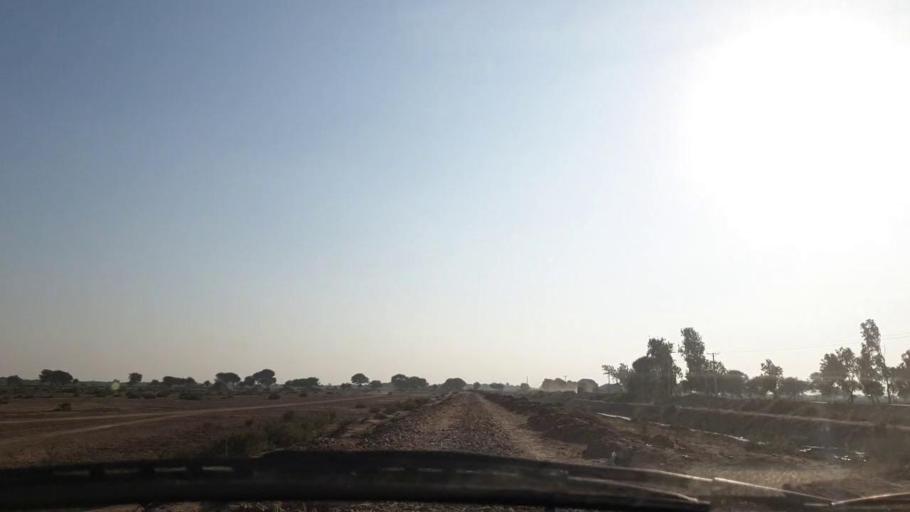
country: PK
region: Sindh
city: Bulri
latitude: 24.8118
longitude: 68.3988
